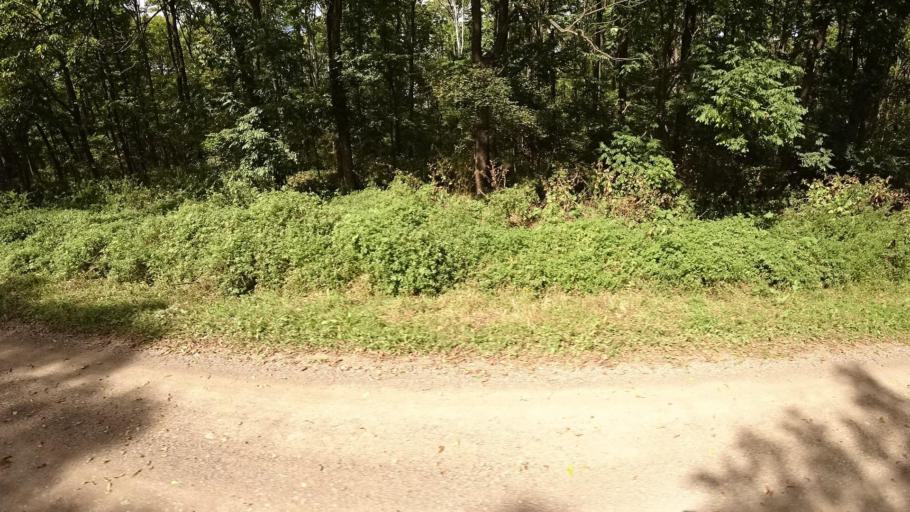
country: RU
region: Primorskiy
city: Yakovlevka
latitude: 44.6597
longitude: 133.7482
